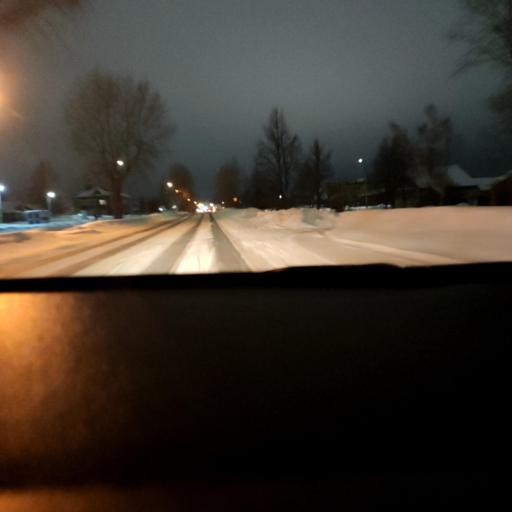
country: RU
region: Tatarstan
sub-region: Chistopol'skiy Rayon
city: Chistopol'
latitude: 55.3563
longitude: 50.6563
